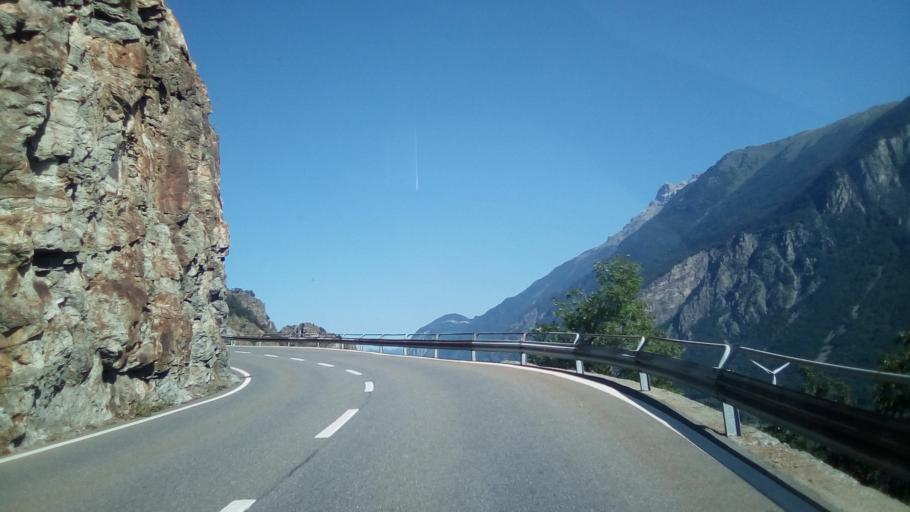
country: CH
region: Valais
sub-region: Saint-Maurice District
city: Vernayaz
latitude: 46.1167
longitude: 7.0477
